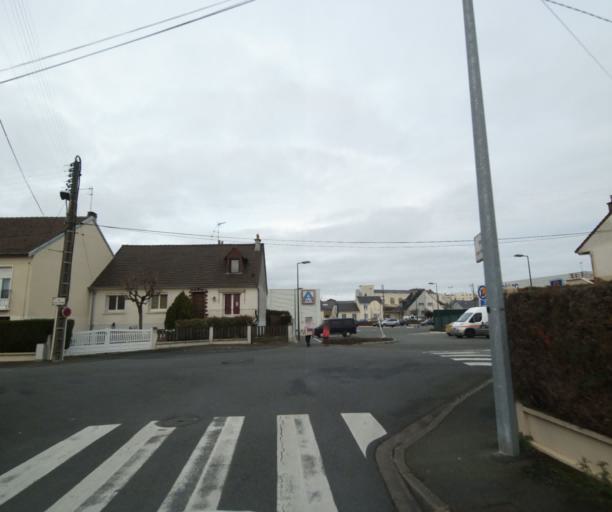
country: FR
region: Pays de la Loire
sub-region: Departement de la Sarthe
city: Le Mans
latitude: 47.9777
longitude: 0.2054
